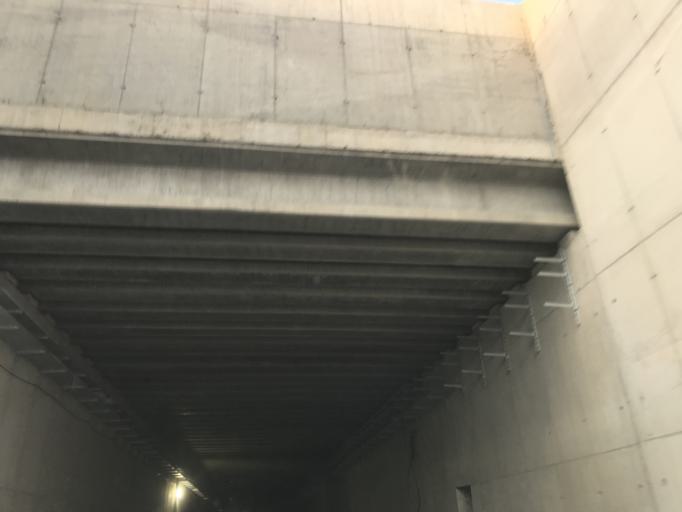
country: TR
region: Istanbul
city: Durusu
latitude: 41.2635
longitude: 28.7148
